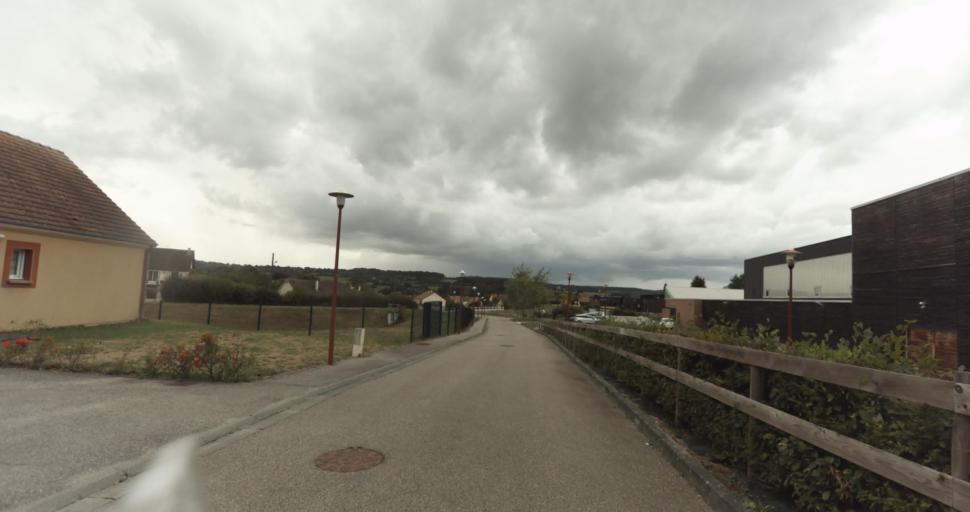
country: FR
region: Lower Normandy
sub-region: Departement de l'Orne
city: Gace
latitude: 48.7891
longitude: 0.3004
